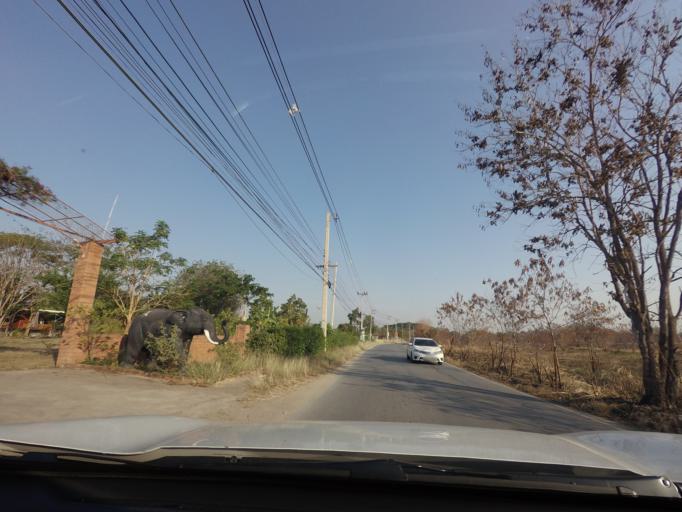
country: TH
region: Nakhon Ratchasima
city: Pak Chong
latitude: 14.6016
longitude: 101.4442
